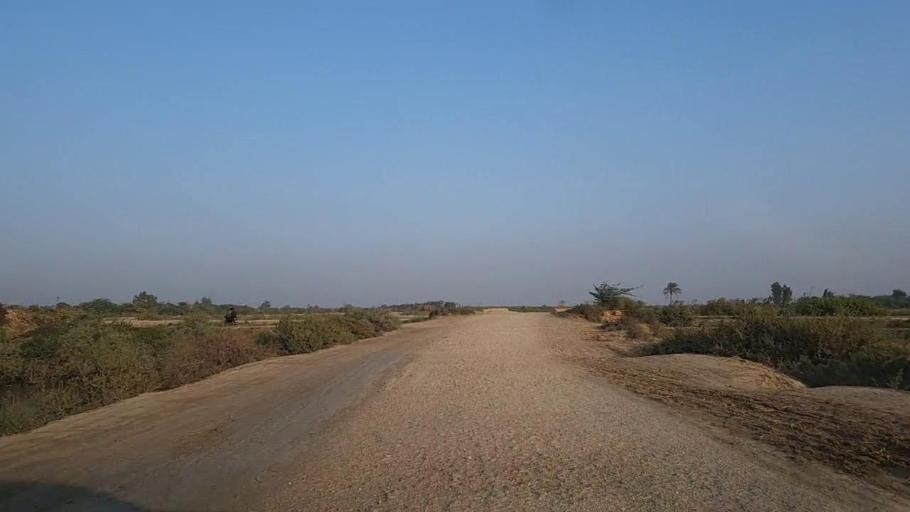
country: PK
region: Sindh
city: Keti Bandar
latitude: 24.2718
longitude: 67.6803
